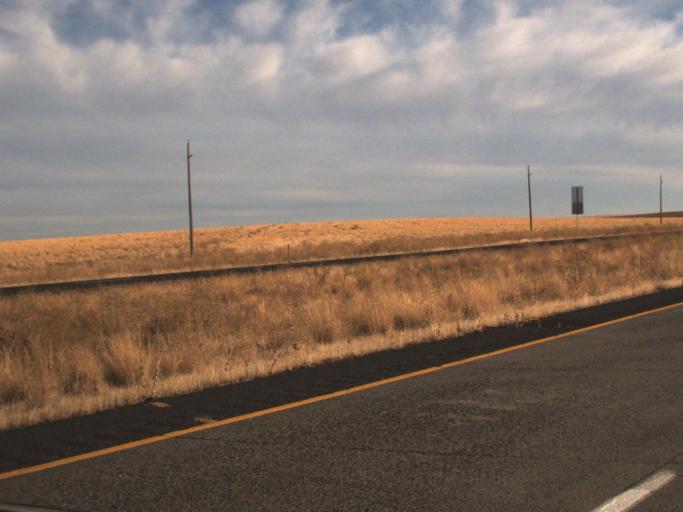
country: US
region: Washington
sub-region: Franklin County
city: Connell
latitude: 46.7303
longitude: -118.8252
